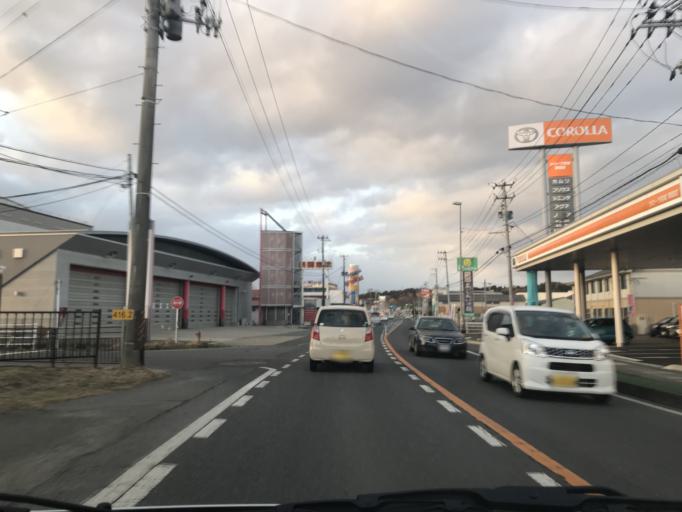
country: JP
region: Miyagi
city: Furukawa
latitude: 38.7441
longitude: 141.0154
